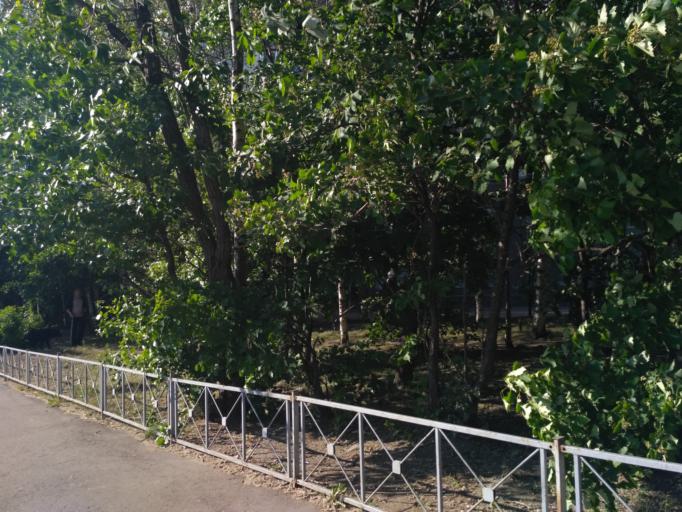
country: RU
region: Leningrad
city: Kalininskiy
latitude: 59.9798
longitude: 30.3816
